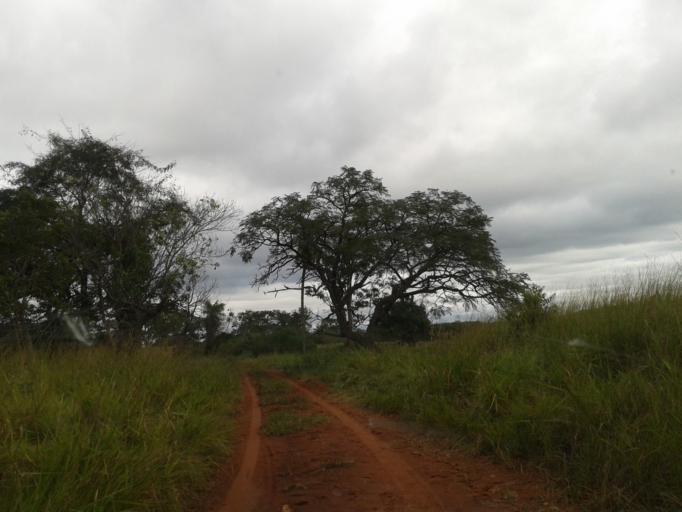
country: BR
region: Minas Gerais
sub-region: Campina Verde
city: Campina Verde
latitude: -19.4876
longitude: -49.6277
